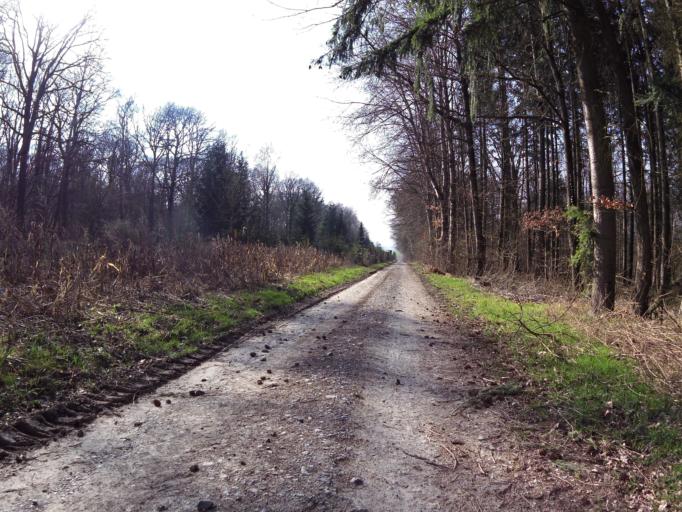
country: DE
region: Bavaria
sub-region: Regierungsbezirk Unterfranken
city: Rottendorf
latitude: 49.8130
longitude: 10.0347
